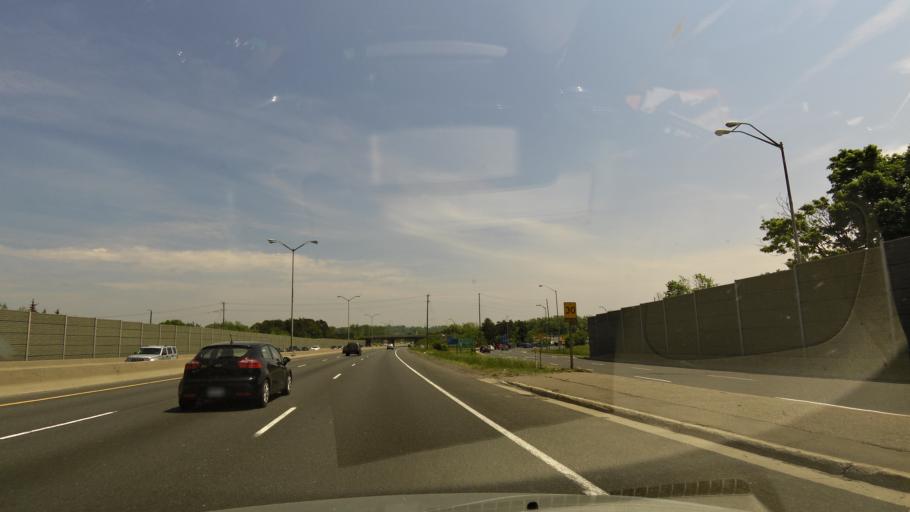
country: CA
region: Ontario
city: Oshawa
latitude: 43.8866
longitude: -78.8333
